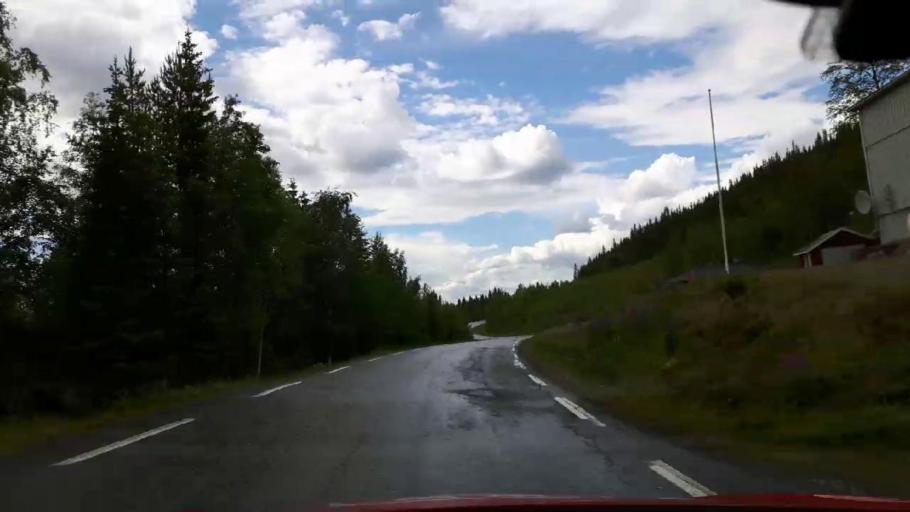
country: NO
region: Nord-Trondelag
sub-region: Lierne
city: Sandvika
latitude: 64.1016
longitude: 14.0051
